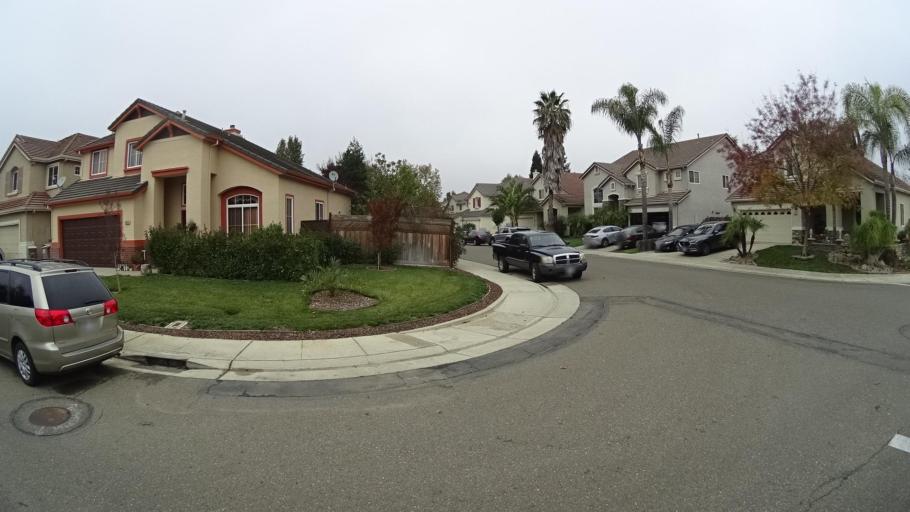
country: US
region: California
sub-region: Sacramento County
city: Elk Grove
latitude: 38.4045
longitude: -121.3463
